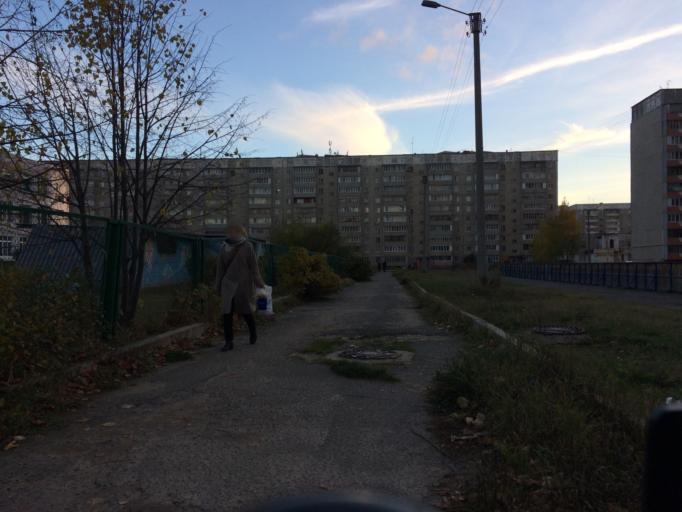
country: RU
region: Mariy-El
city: Yoshkar-Ola
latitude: 56.6362
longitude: 47.9291
